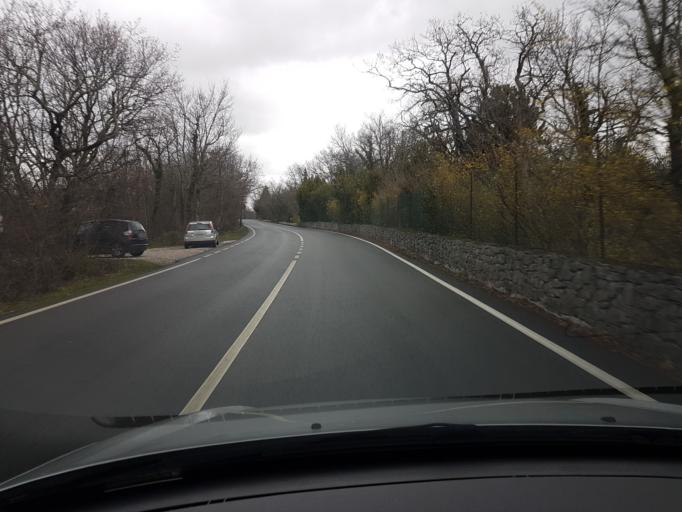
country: IT
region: Friuli Venezia Giulia
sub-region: Provincia di Trieste
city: Sgonico
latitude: 45.7328
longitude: 13.7284
